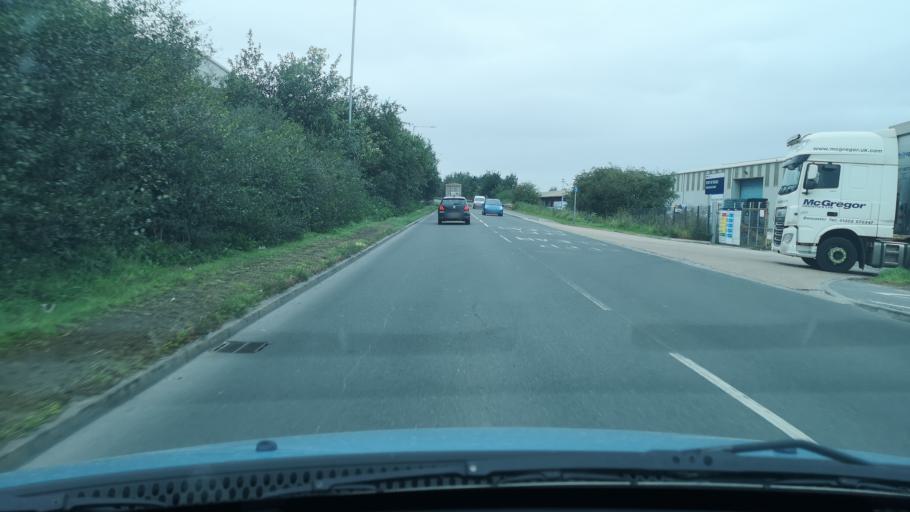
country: GB
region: England
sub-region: East Riding of Yorkshire
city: Goole
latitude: 53.6992
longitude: -0.8768
